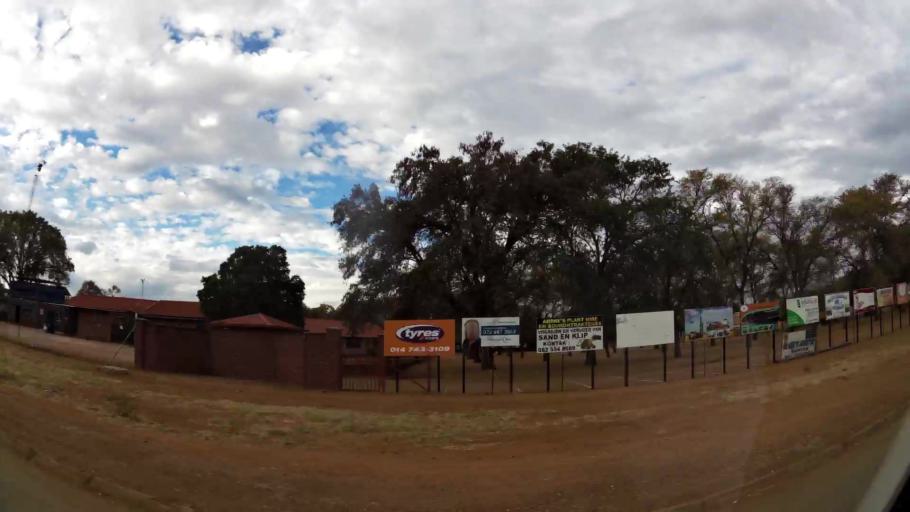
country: ZA
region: Limpopo
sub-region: Waterberg District Municipality
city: Modimolle
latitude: -24.5141
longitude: 28.7065
